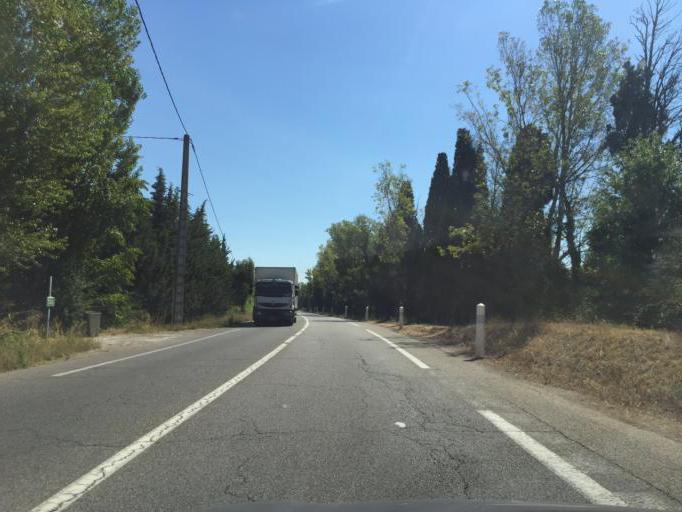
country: FR
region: Provence-Alpes-Cote d'Azur
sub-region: Departement du Vaucluse
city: Le Thor
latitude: 43.8813
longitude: 5.0116
